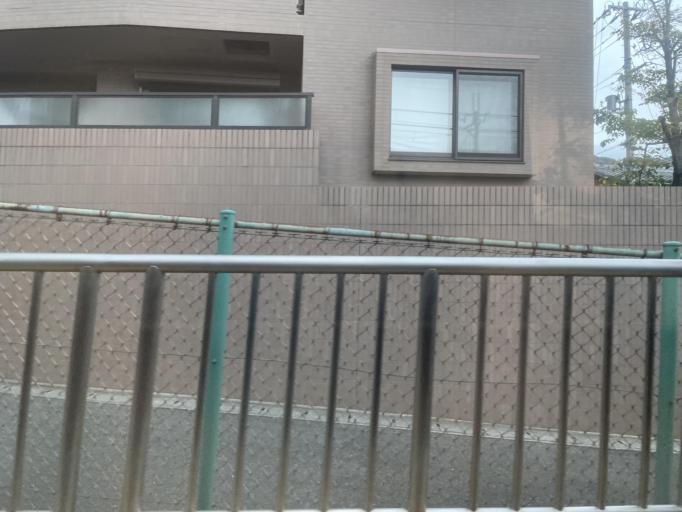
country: JP
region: Hyogo
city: Ashiya
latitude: 34.7292
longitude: 135.2760
